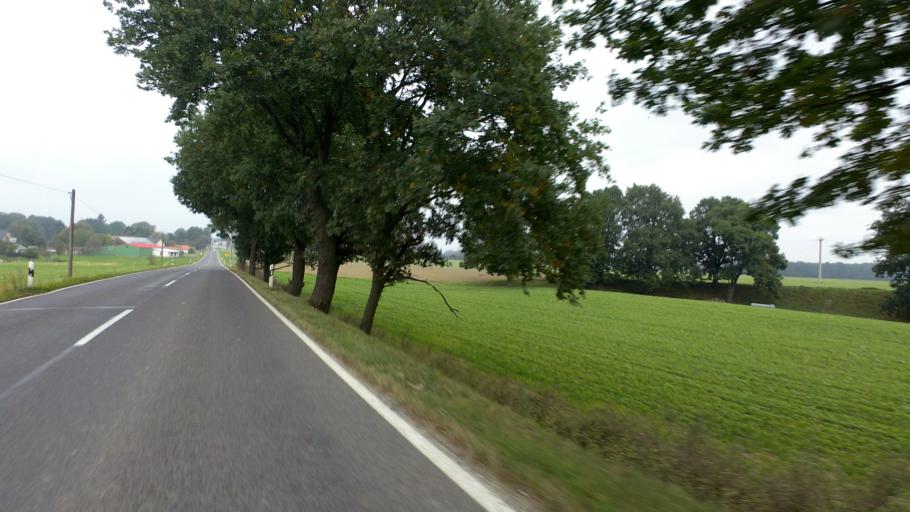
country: DE
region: Saxony
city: Arnsdorf
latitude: 51.0839
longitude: 14.0237
